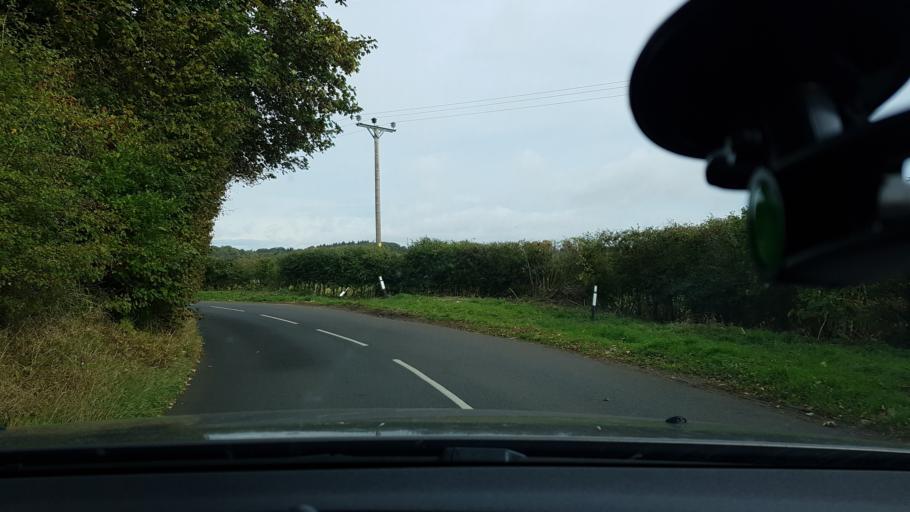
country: GB
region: England
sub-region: West Berkshire
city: Kintbury
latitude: 51.4048
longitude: -1.4746
